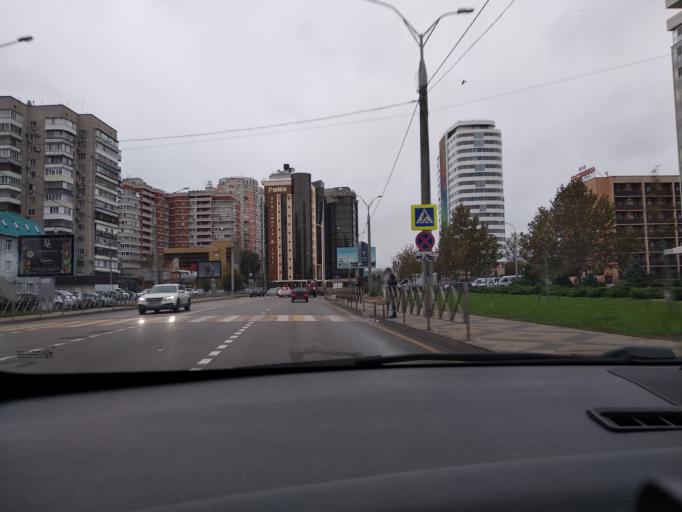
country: RU
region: Krasnodarskiy
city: Krasnodar
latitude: 45.0195
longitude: 38.9597
